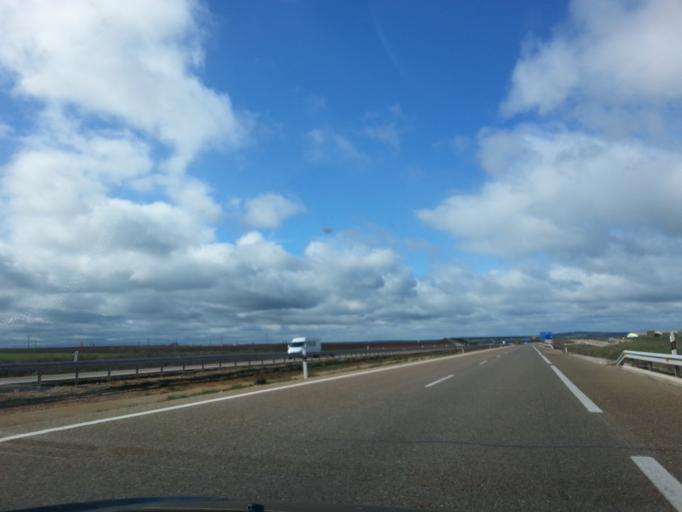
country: ES
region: Castille and Leon
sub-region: Provincia de Salamanca
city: Robliza de Cojos
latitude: 40.8839
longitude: -5.9609
